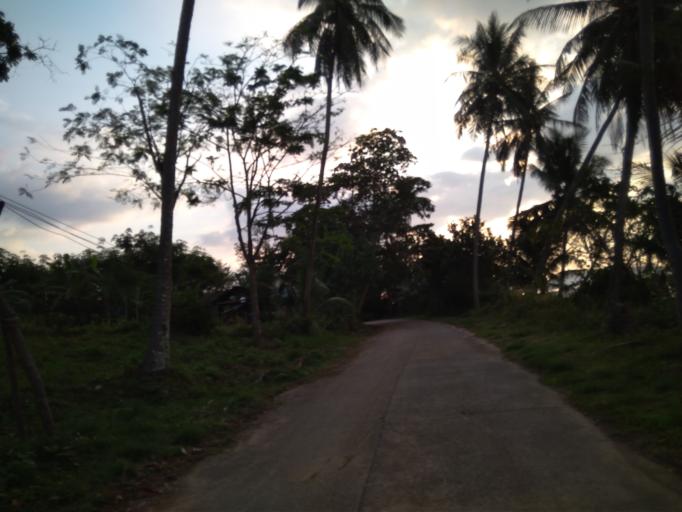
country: TH
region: Phangnga
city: Ko Yao
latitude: 8.1653
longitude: 98.6134
